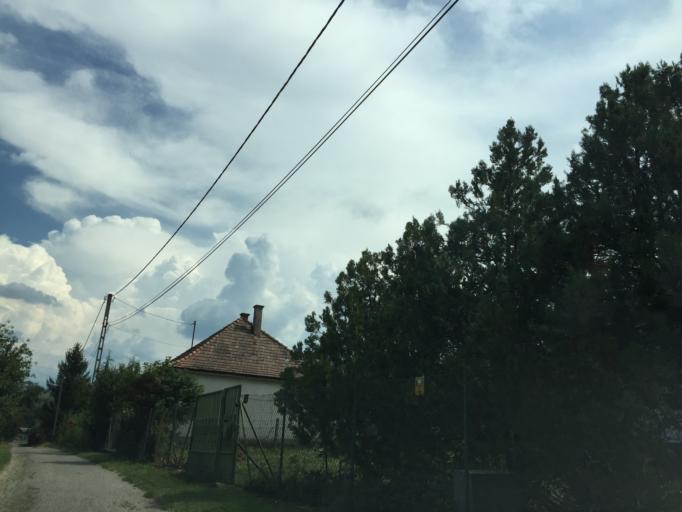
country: HU
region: Nograd
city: Nagyoroszi
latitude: 47.9756
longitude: 19.0979
